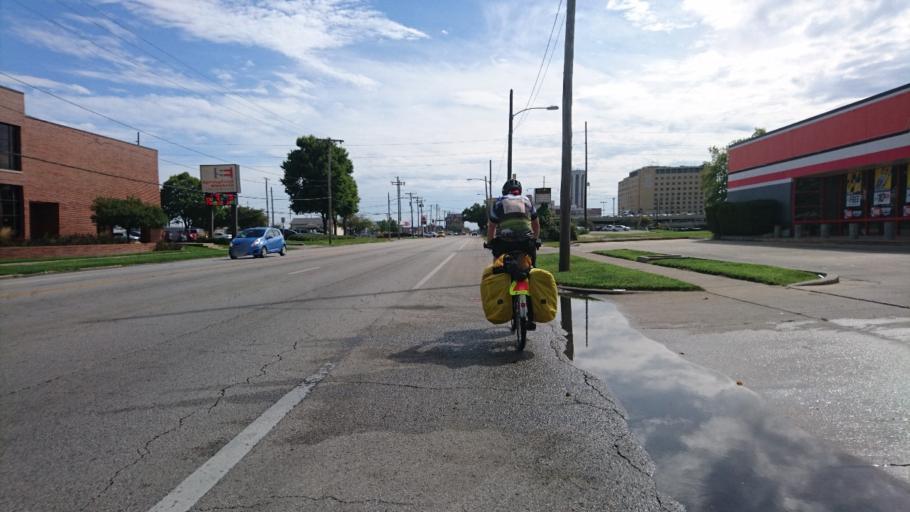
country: US
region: Illinois
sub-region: Sangamon County
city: Springfield
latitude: 39.8095
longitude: -89.6435
